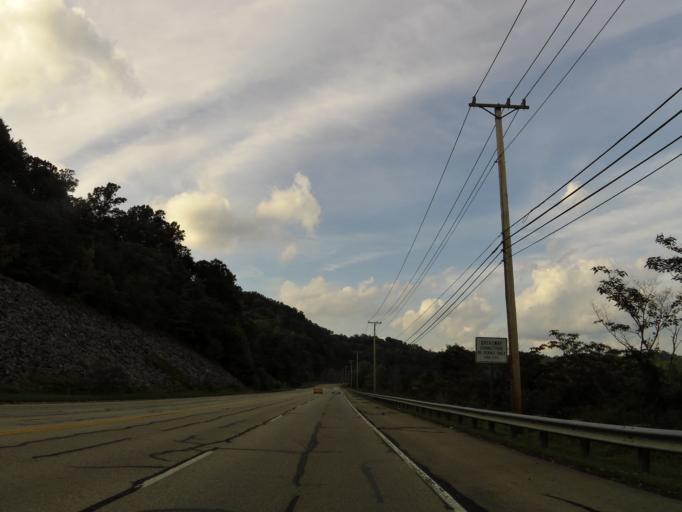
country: US
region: Tennessee
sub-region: Anderson County
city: Clinton
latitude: 36.0643
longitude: -84.1971
